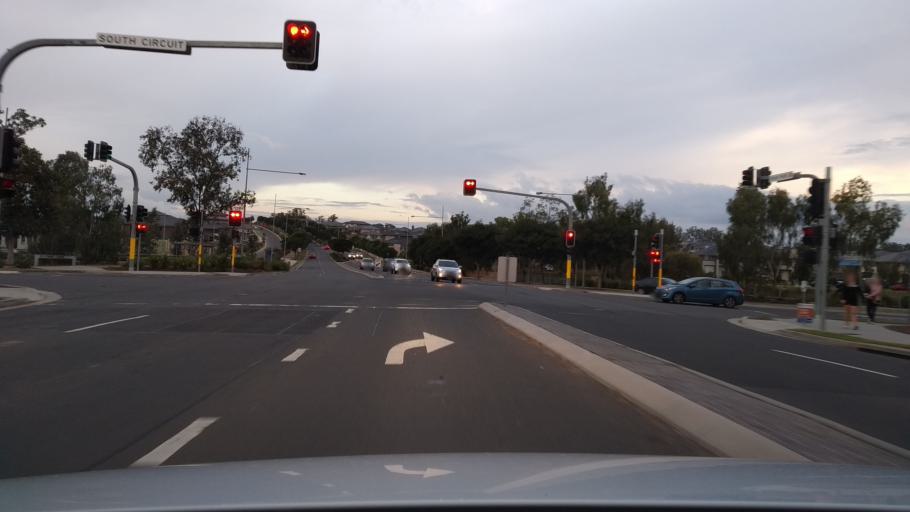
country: AU
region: New South Wales
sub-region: Camden
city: Narellan
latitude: -34.0078
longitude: 150.7393
